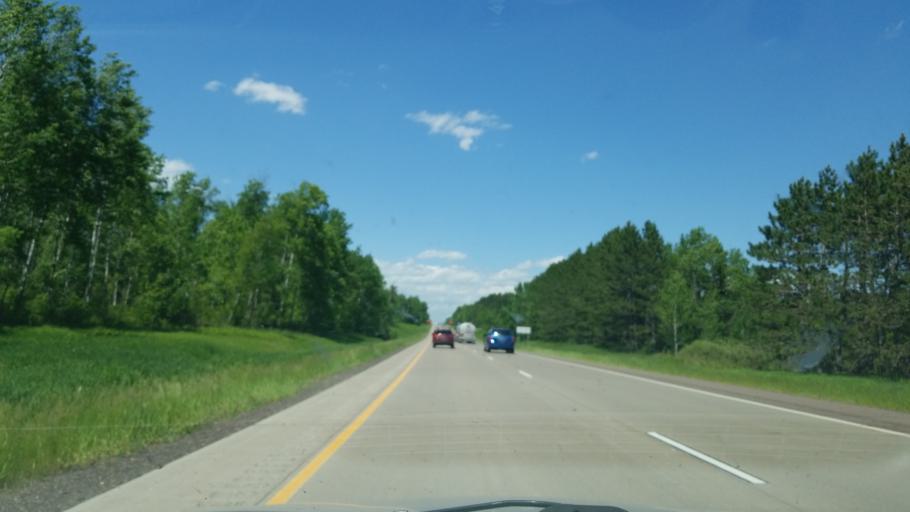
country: US
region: Minnesota
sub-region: Pine County
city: Sandstone
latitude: 46.2354
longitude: -92.8253
